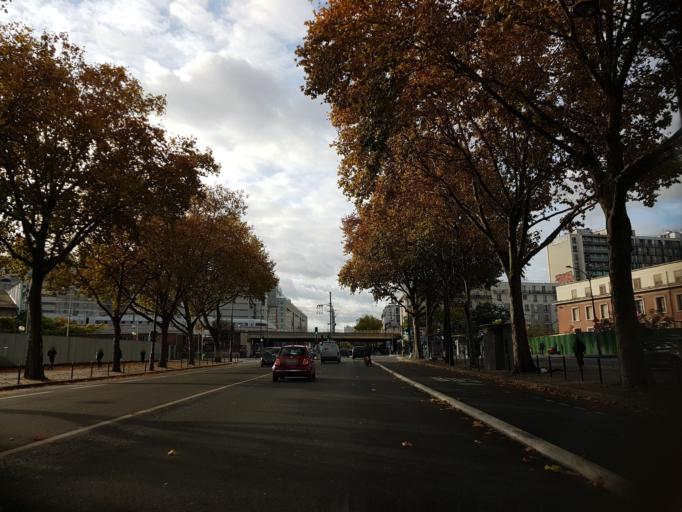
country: FR
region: Ile-de-France
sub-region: Departement de Seine-Saint-Denis
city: Aubervilliers
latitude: 48.8992
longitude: 2.3872
